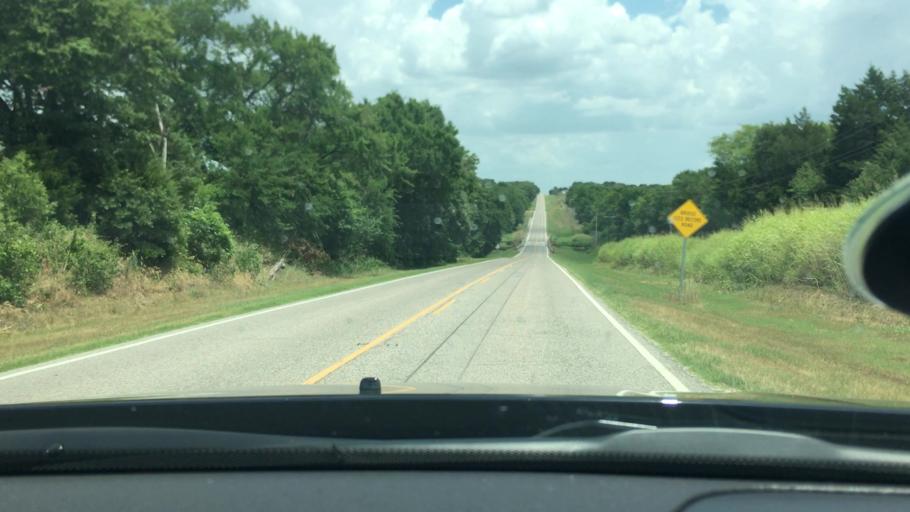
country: US
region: Oklahoma
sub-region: Love County
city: Marietta
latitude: 33.9839
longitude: -96.9785
